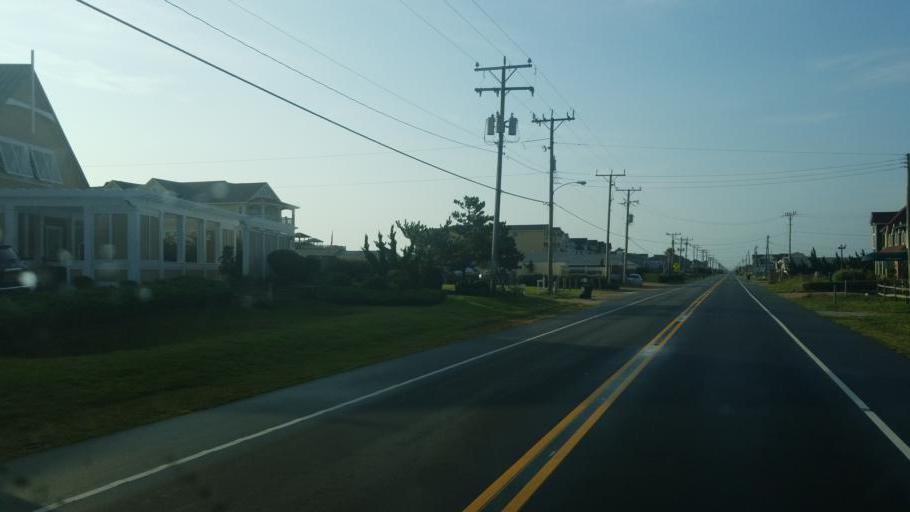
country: US
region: North Carolina
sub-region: Dare County
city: Kill Devil Hills
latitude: 36.0124
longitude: -75.6564
